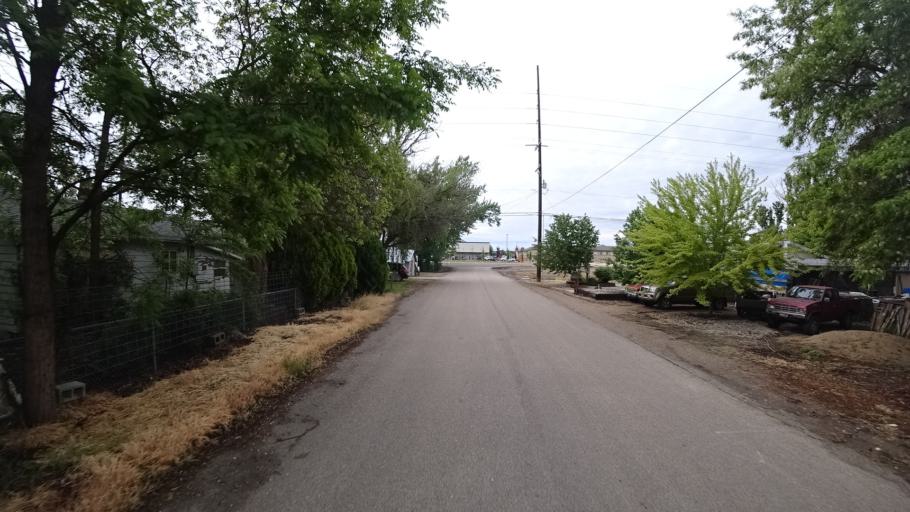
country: US
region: Idaho
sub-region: Ada County
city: Star
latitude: 43.6928
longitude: -116.4956
